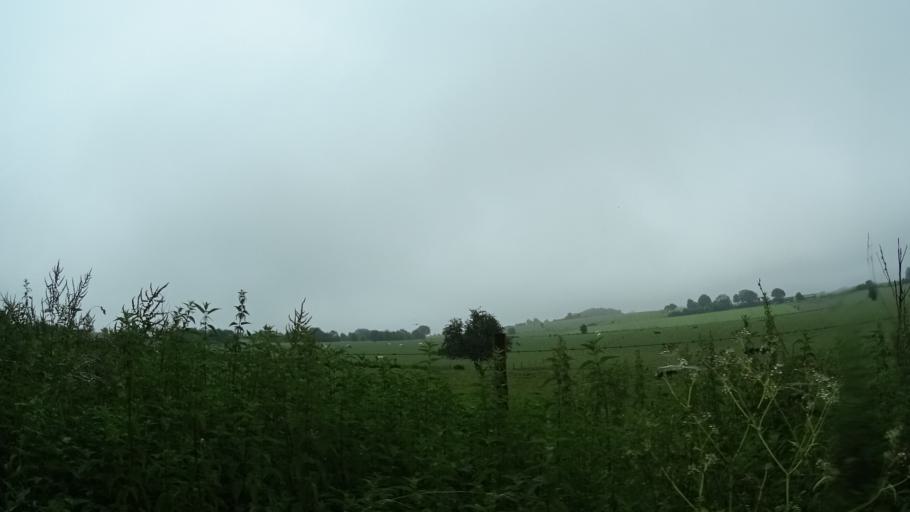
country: BE
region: Wallonia
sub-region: Province de Namur
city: Bievre
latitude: 49.9954
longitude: 5.0123
